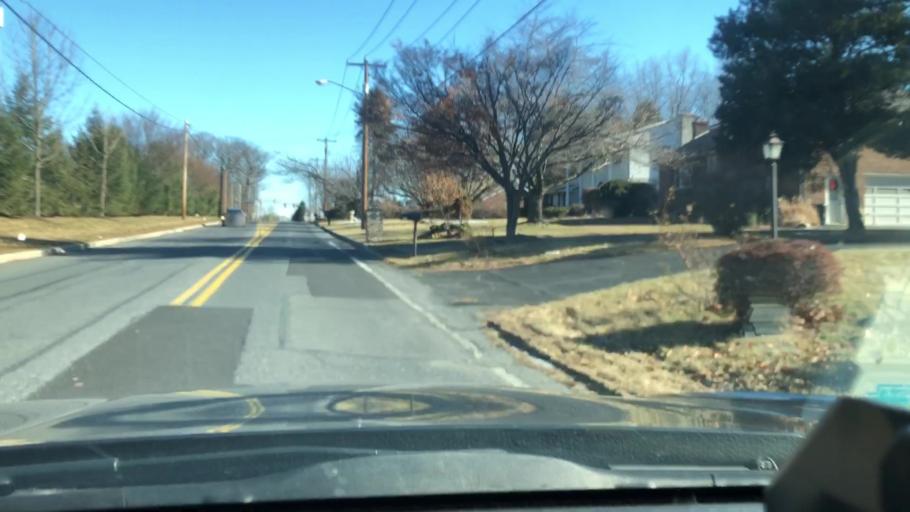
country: US
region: Pennsylvania
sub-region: Northampton County
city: Bethlehem
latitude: 40.6521
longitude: -75.4010
